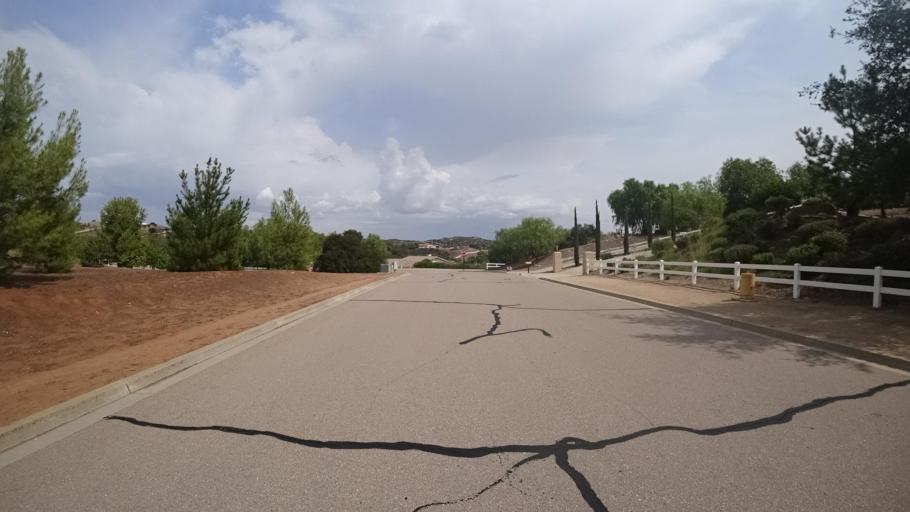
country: US
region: California
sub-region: San Diego County
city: Ramona
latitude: 32.9954
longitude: -116.8943
